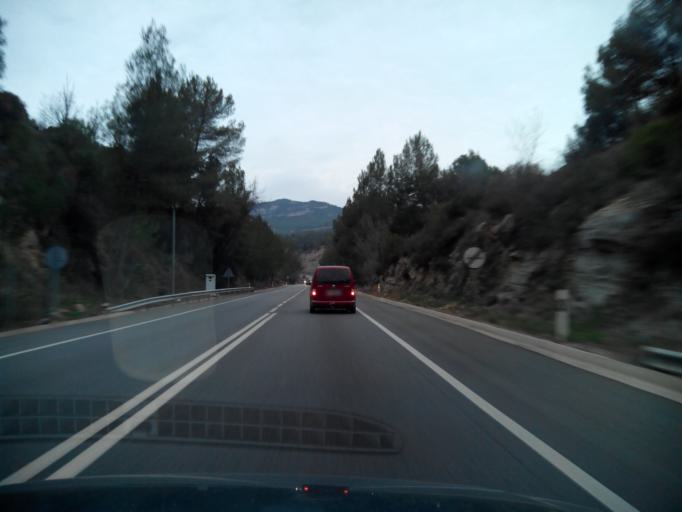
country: ES
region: Catalonia
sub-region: Provincia de Barcelona
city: Monistrol de Montserrat
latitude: 41.6220
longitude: 1.8602
